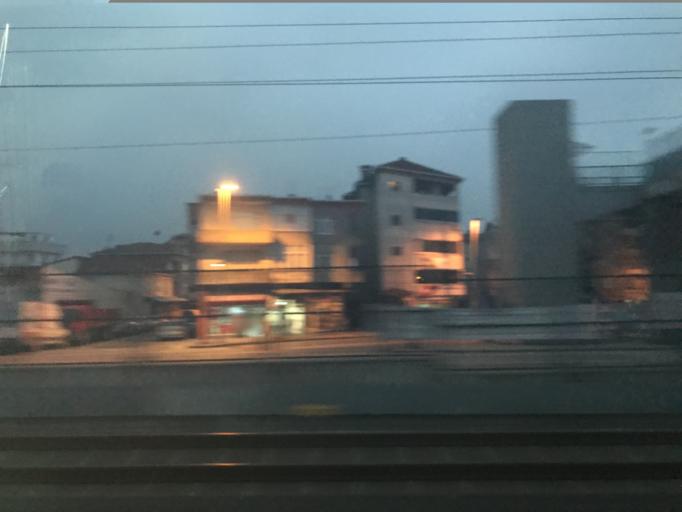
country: TR
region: Kocaeli
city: Darica
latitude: 40.7857
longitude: 29.4047
